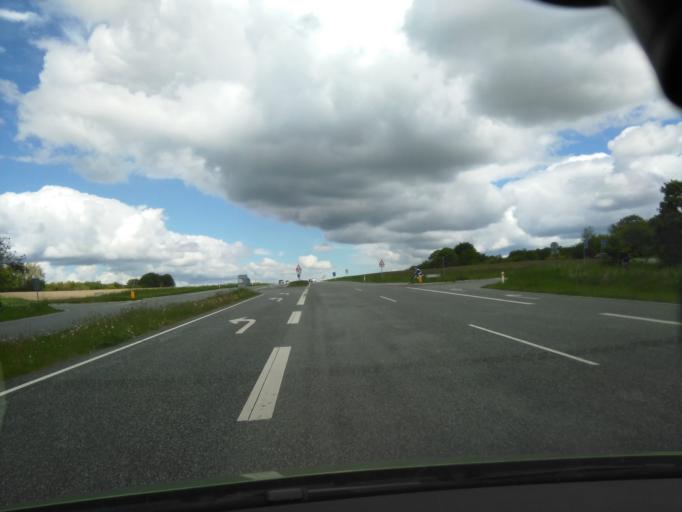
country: DK
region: Central Jutland
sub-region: Arhus Kommune
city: Solbjerg
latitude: 56.0520
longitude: 10.0840
